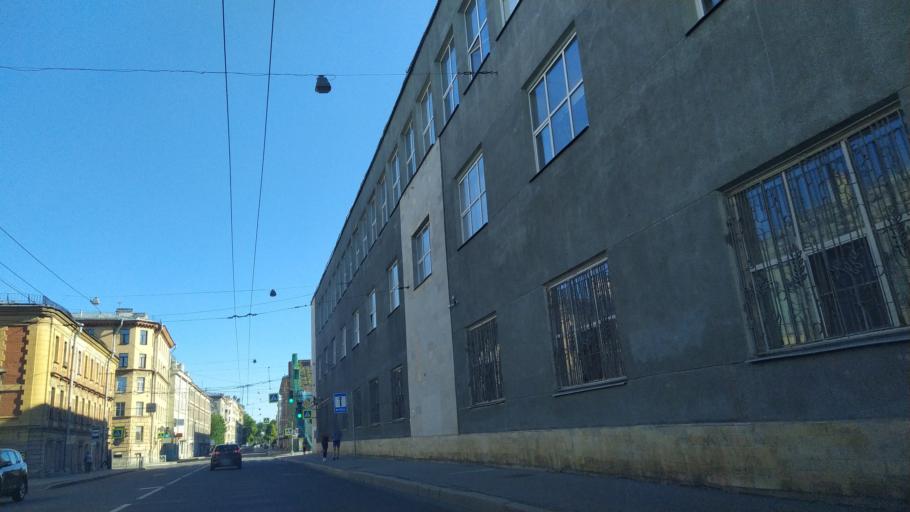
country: RU
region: Leningrad
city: Sampsonievskiy
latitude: 59.9676
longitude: 30.3424
